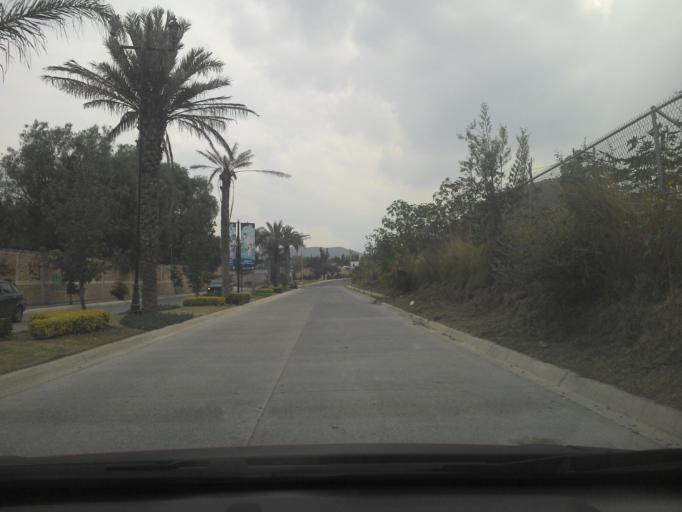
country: MX
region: Jalisco
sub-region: Tlajomulco de Zuniga
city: Lomas de San Agustin
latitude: 20.5307
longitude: -103.4748
